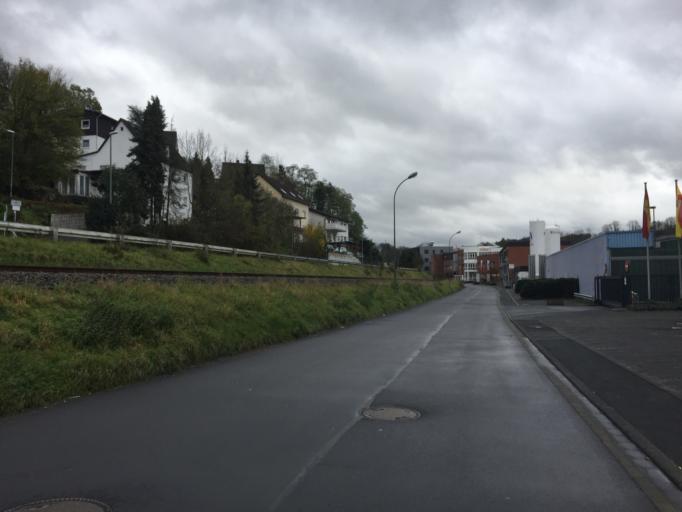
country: DE
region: Hesse
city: Dillenburg
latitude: 50.7474
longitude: 8.2776
